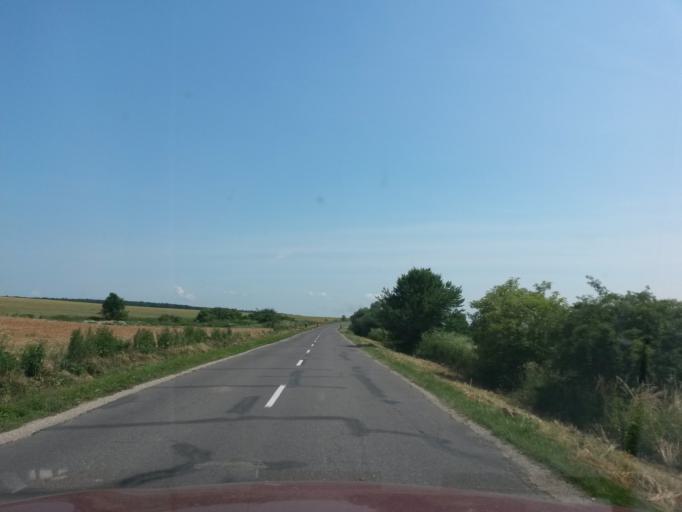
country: SK
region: Kosicky
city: Moldava nad Bodvou
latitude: 48.6458
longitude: 21.0075
